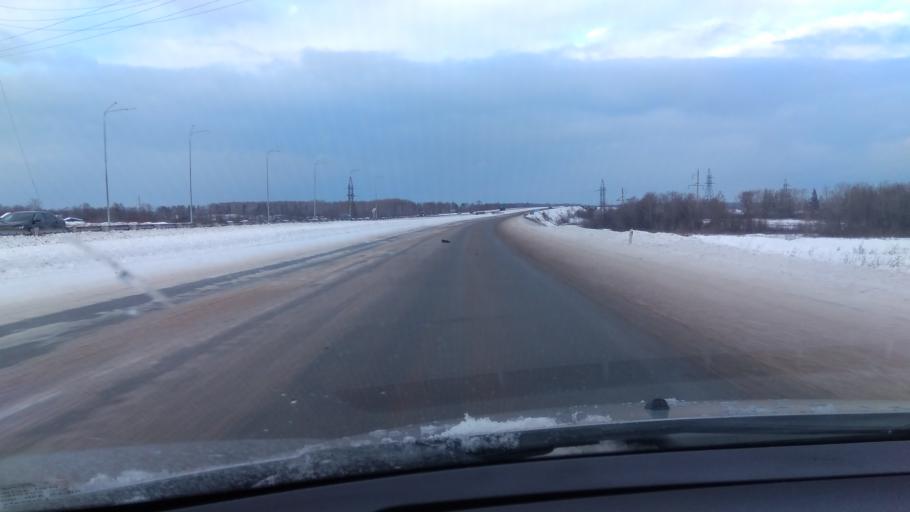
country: RU
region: Sverdlovsk
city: Tsementnyy
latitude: 57.4979
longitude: 60.1747
